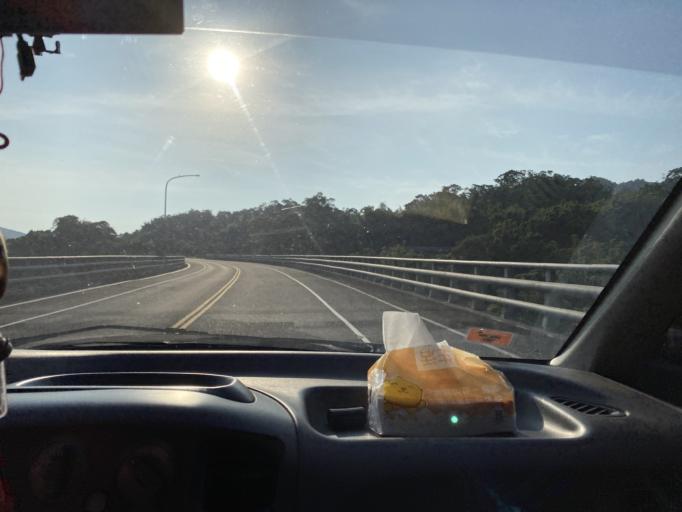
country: TW
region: Taiwan
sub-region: Keelung
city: Keelung
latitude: 25.0350
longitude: 121.8573
